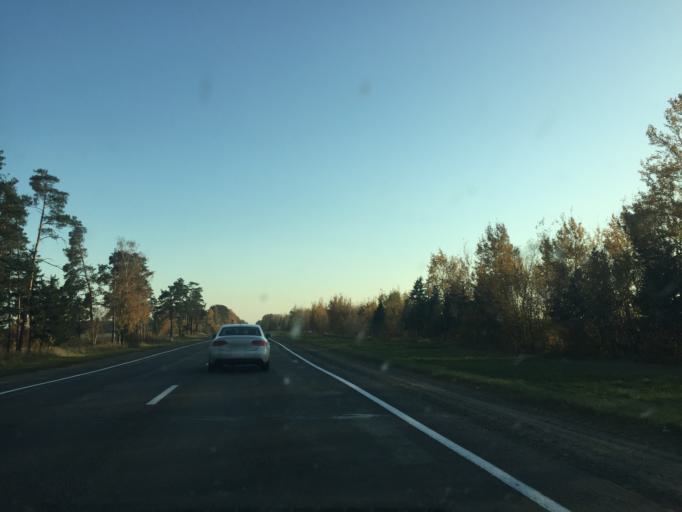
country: BY
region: Mogilev
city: Poselok Voskhod
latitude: 53.7433
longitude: 30.3659
